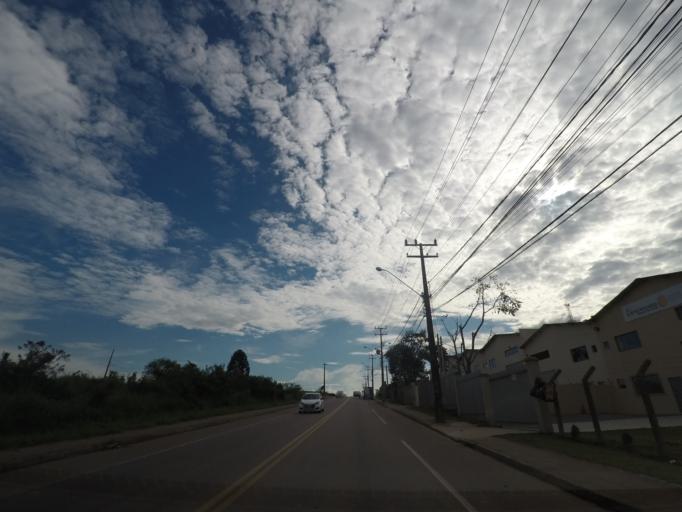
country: BR
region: Parana
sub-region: Araucaria
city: Araucaria
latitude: -25.6411
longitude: -49.3090
